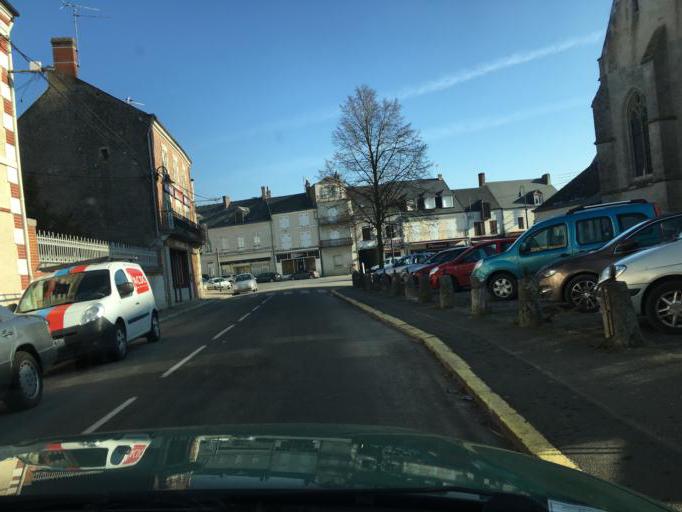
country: FR
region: Centre
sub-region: Departement du Loiret
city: Patay
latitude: 48.0477
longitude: 1.6946
